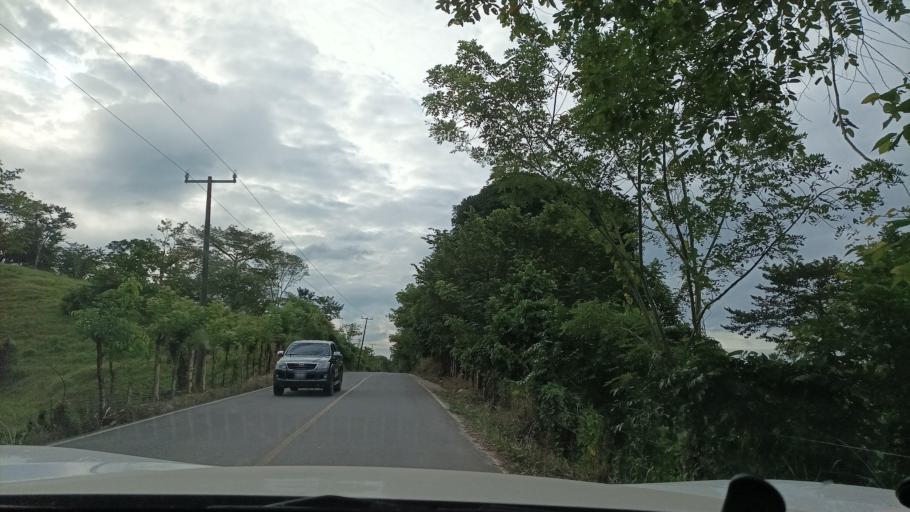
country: MX
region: Veracruz
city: Hidalgotitlan
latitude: 17.7405
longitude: -94.4894
